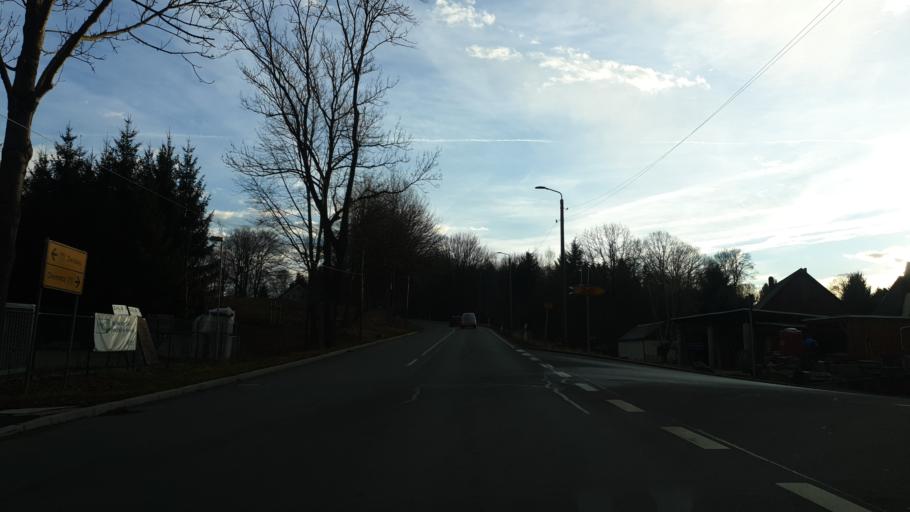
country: DE
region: Saxony
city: Kirchberg
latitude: 50.7909
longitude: 12.7620
